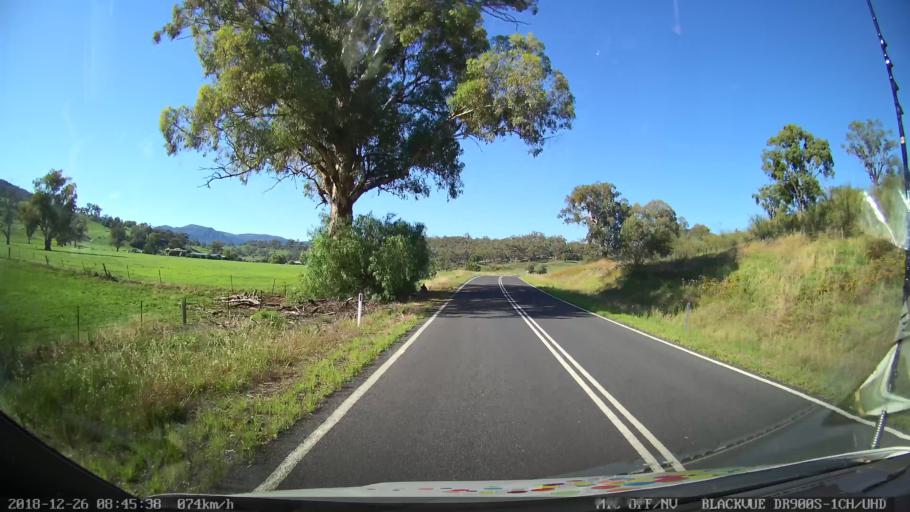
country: AU
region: New South Wales
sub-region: Mid-Western Regional
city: Kandos
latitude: -32.5274
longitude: 150.0868
